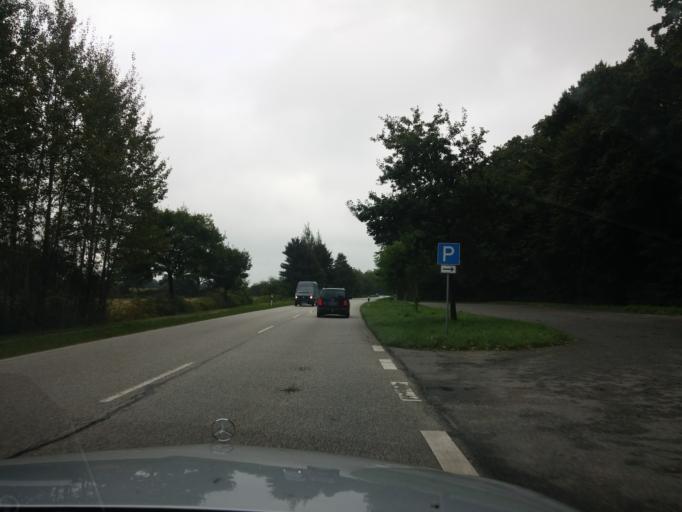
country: DE
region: Schleswig-Holstein
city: Silberstedt
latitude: 54.5160
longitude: 9.3524
